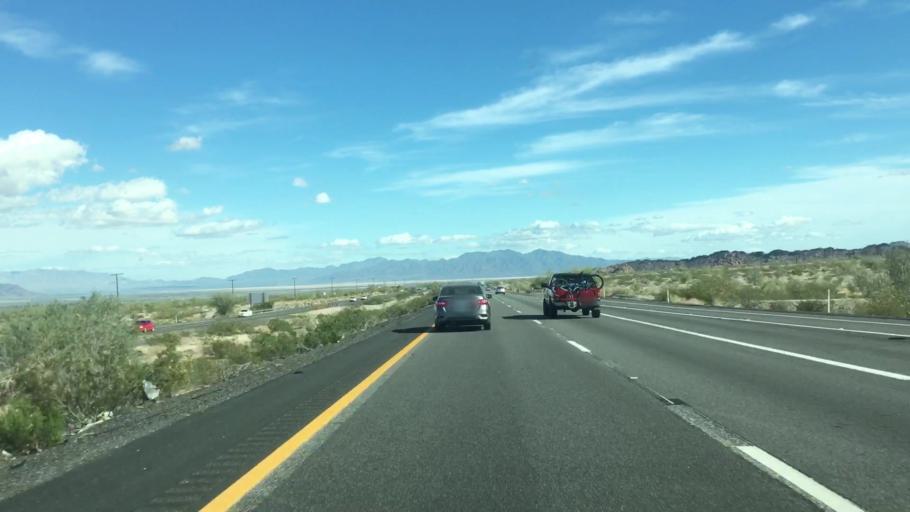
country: US
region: California
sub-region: Imperial County
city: Niland
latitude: 33.7023
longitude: -115.4506
